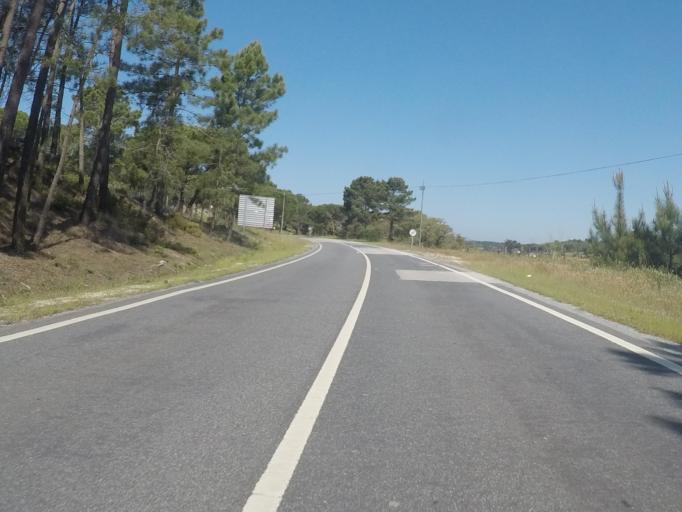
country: PT
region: Setubal
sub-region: Grandola
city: Grandola
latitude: 38.2991
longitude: -8.7266
